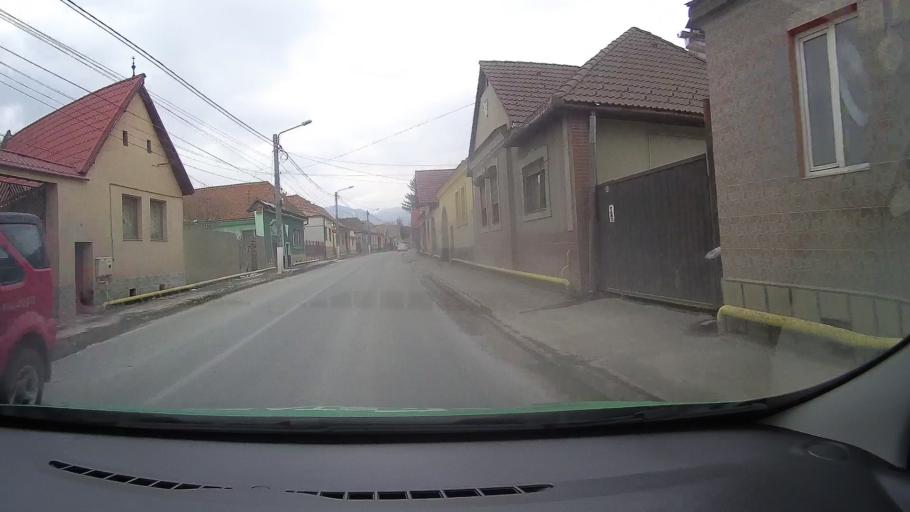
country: RO
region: Brasov
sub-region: Comuna Zarnesti
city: Tohanu Nou
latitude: 45.5738
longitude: 25.3599
